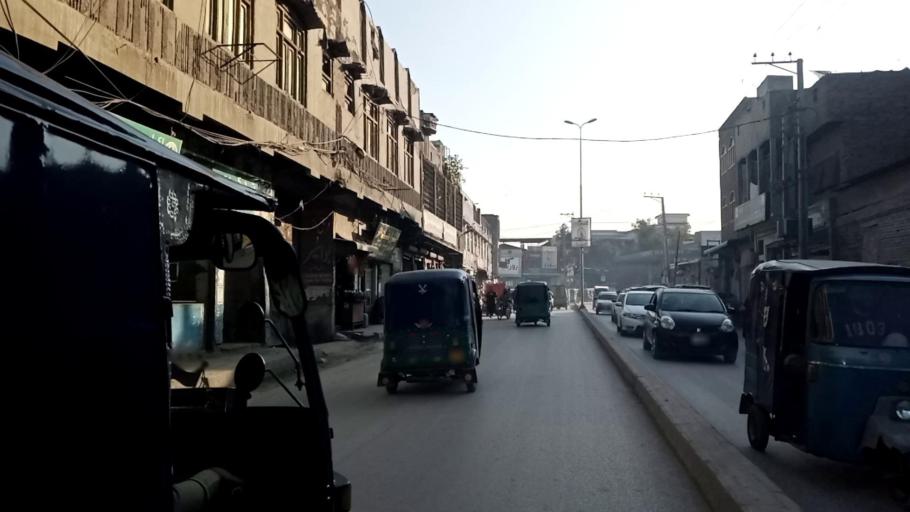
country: PK
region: Khyber Pakhtunkhwa
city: Peshawar
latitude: 34.0059
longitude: 71.5845
